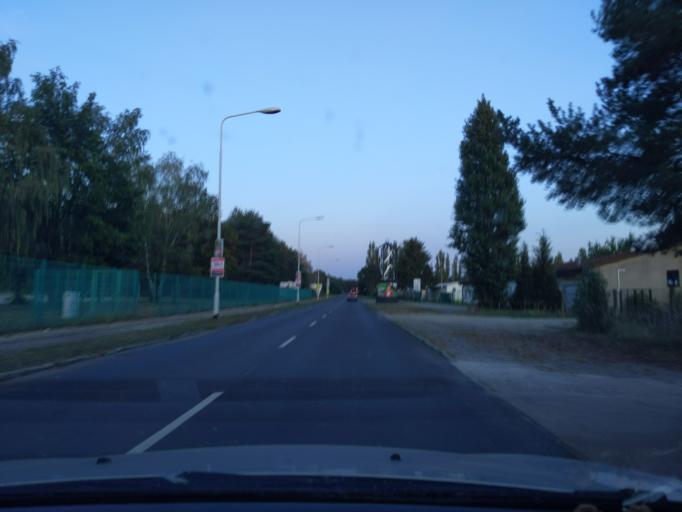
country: DE
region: Saxony
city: Hoyerswerda
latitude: 51.4299
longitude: 14.2914
